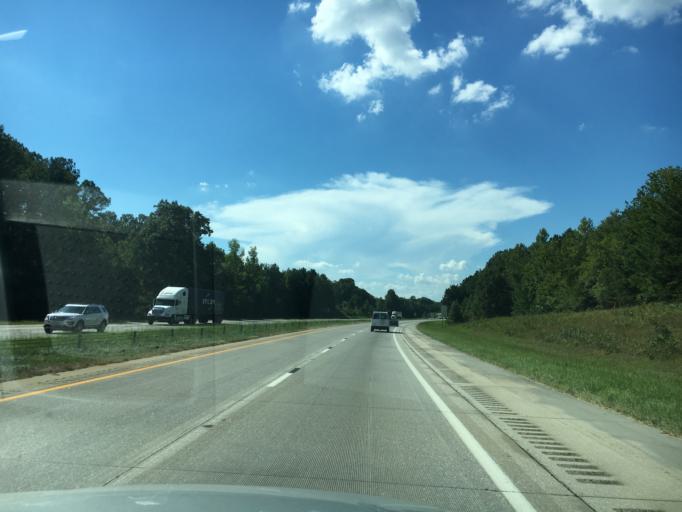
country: US
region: South Carolina
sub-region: Laurens County
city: Watts Mills
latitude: 34.5563
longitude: -82.0166
